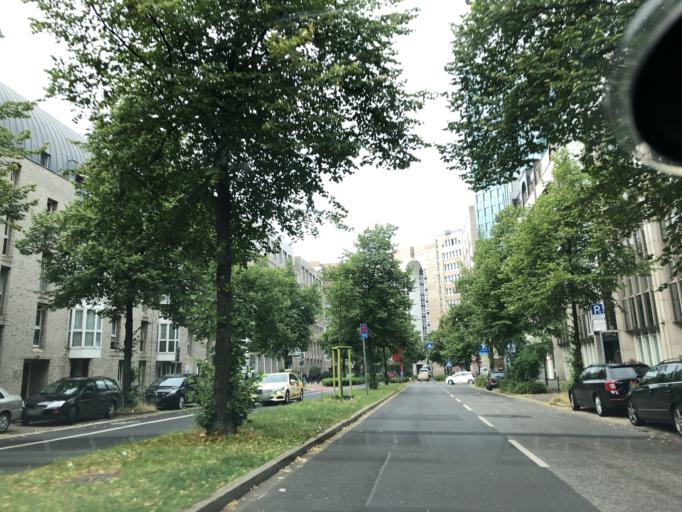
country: DE
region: North Rhine-Westphalia
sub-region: Regierungsbezirk Dusseldorf
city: Dusseldorf
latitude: 51.2204
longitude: 6.7981
